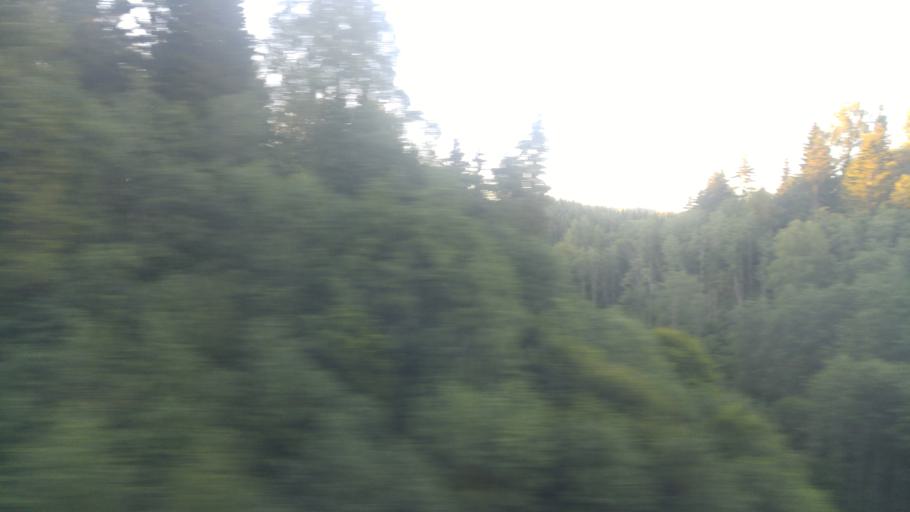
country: NO
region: Akershus
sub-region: Eidsvoll
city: Eidsvoll
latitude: 60.3152
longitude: 11.2371
